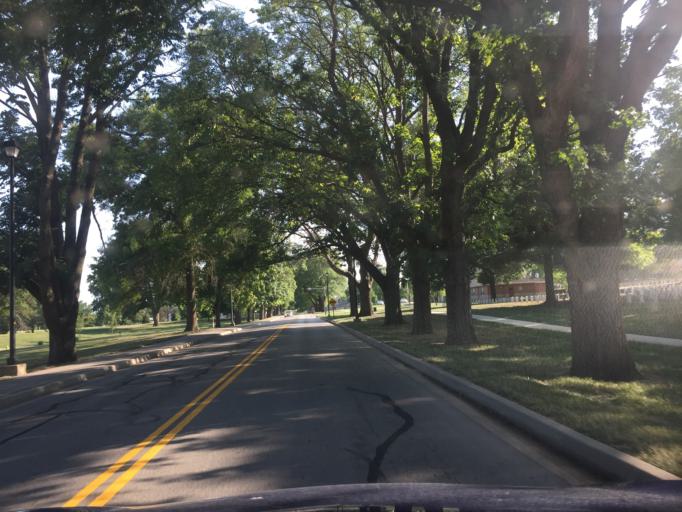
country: US
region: Kansas
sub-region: Leavenworth County
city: Leavenworth
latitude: 39.3499
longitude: -94.9288
